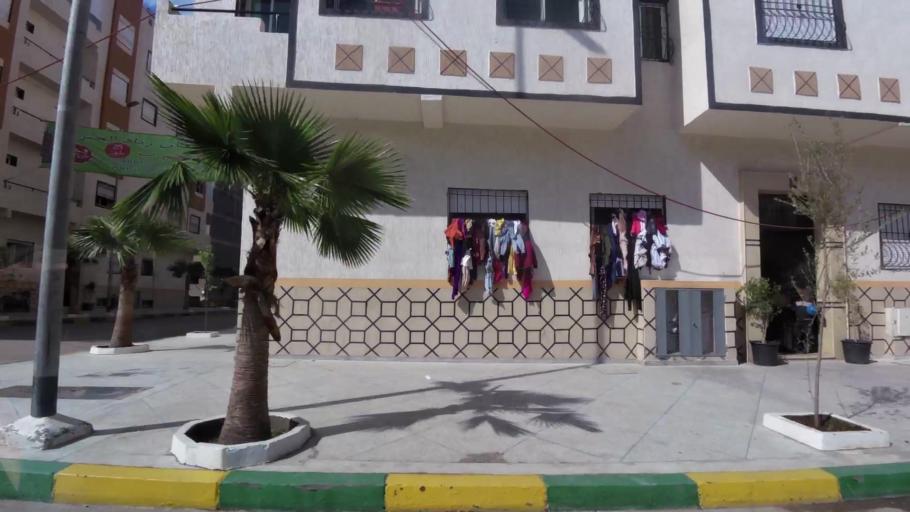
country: MA
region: Chaouia-Ouardigha
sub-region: Settat Province
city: Berrechid
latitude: 33.2599
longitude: -7.5635
